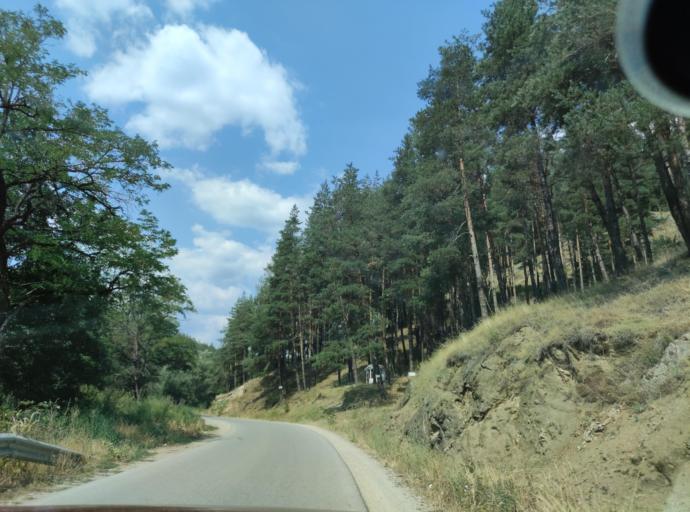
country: BG
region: Blagoevgrad
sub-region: Obshtina Belitsa
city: Belitsa
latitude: 41.9583
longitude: 23.5566
